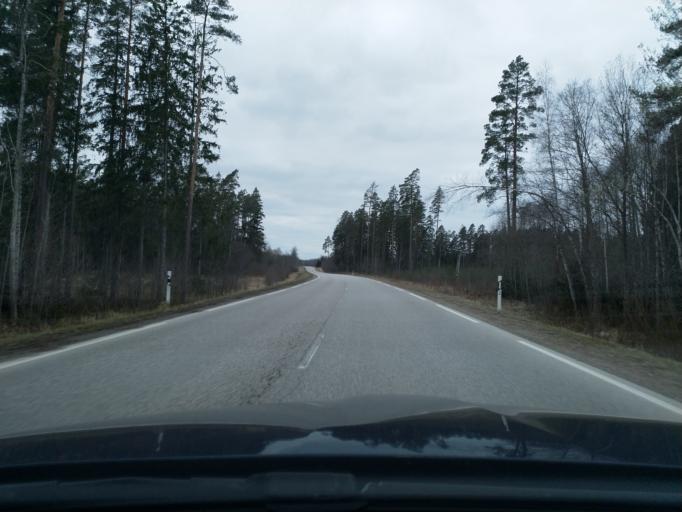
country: LV
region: Kuldigas Rajons
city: Kuldiga
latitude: 56.9556
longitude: 22.1354
